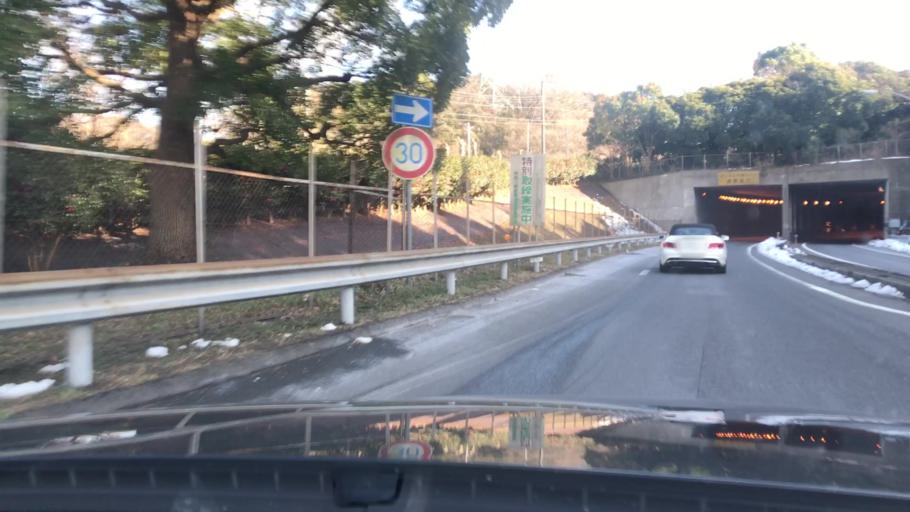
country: JP
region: Kanagawa
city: Zushi
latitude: 35.2943
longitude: 139.6175
